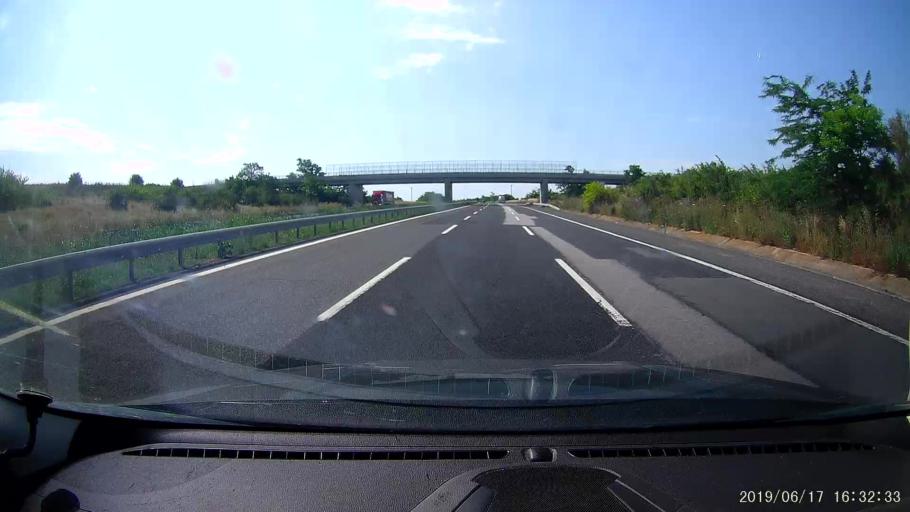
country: TR
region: Kirklareli
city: Buyukkaristiran
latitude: 41.3705
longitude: 27.5969
